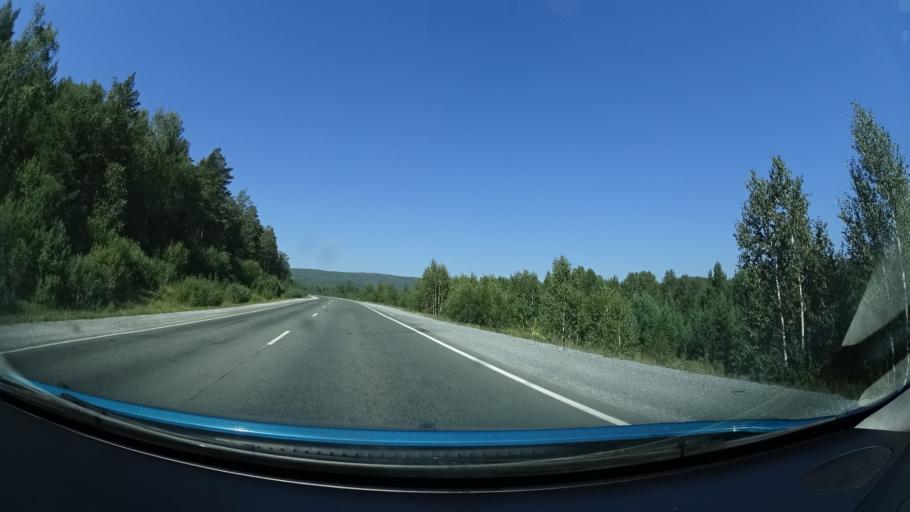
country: RU
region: Bashkortostan
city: Abzakovo
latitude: 53.8554
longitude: 58.5750
